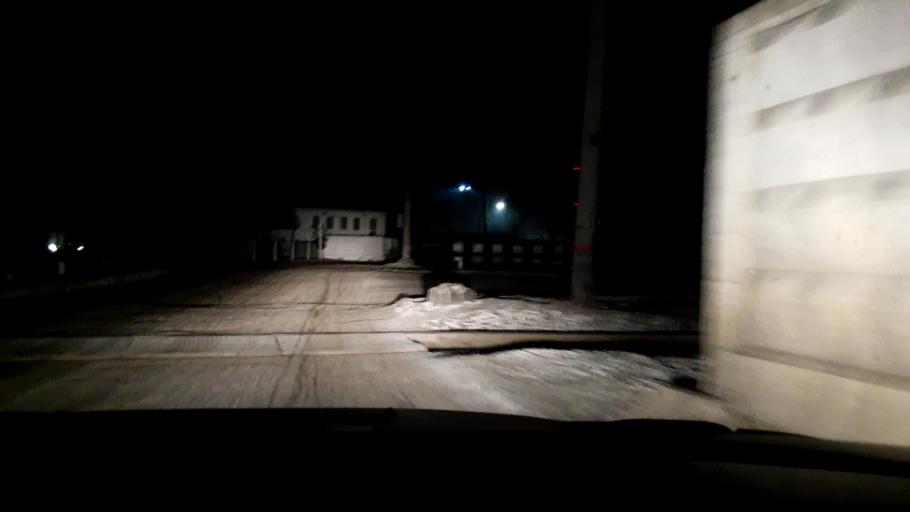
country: RU
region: Nizjnij Novgorod
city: Gorbatovka
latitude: 56.2767
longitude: 43.8399
